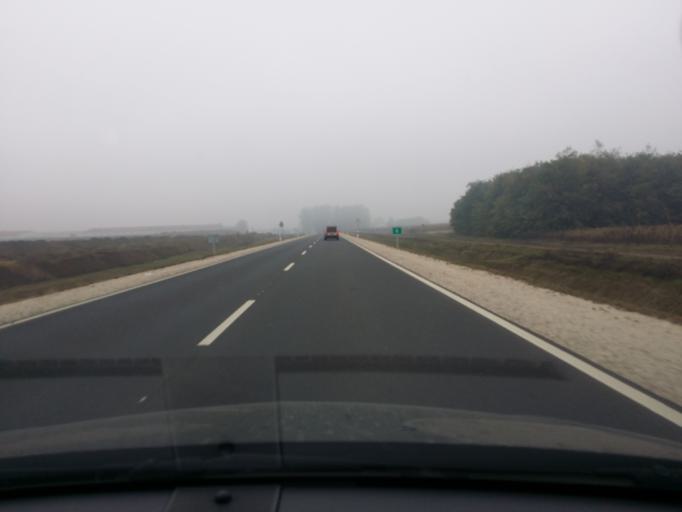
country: HU
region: Szabolcs-Szatmar-Bereg
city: Nyiregyhaza
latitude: 47.9497
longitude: 21.6539
